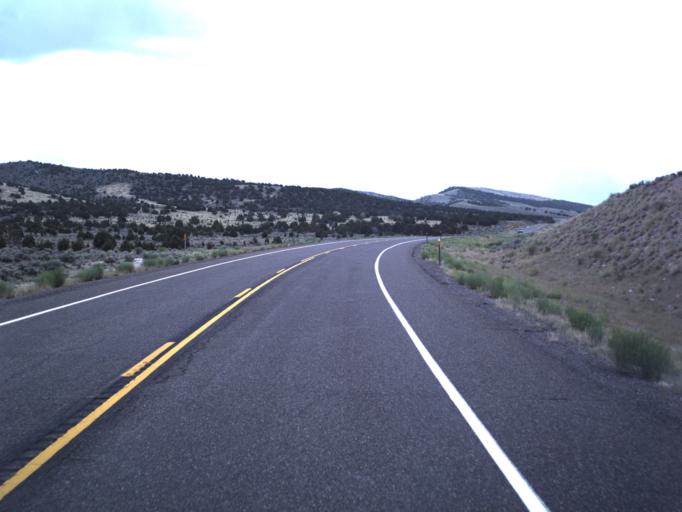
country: US
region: Utah
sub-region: Wayne County
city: Loa
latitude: 38.5486
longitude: -111.8351
